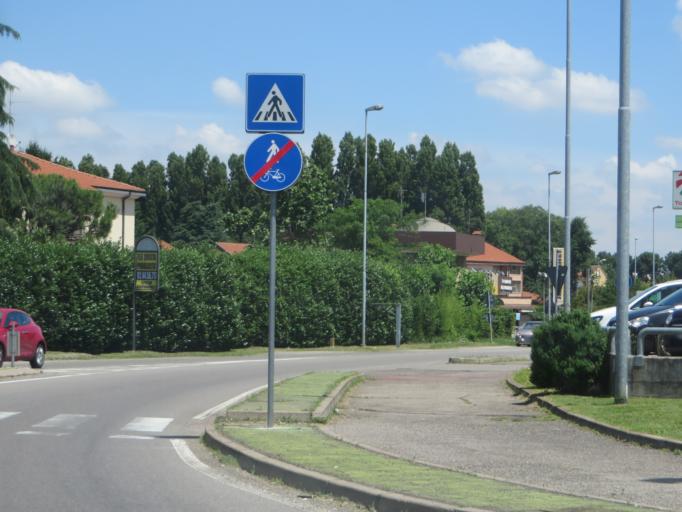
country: IT
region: Lombardy
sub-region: Citta metropolitana di Milano
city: Bareggio
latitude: 45.4847
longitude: 8.9908
